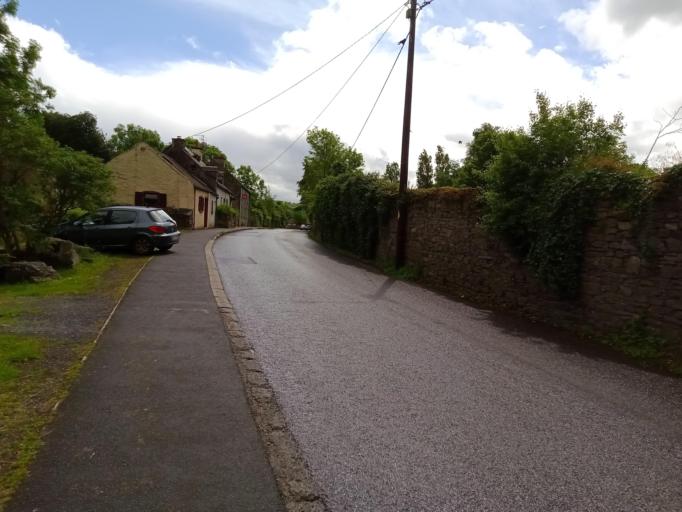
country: IE
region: Leinster
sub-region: Kilkenny
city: Thomastown
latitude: 52.5223
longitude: -7.1374
